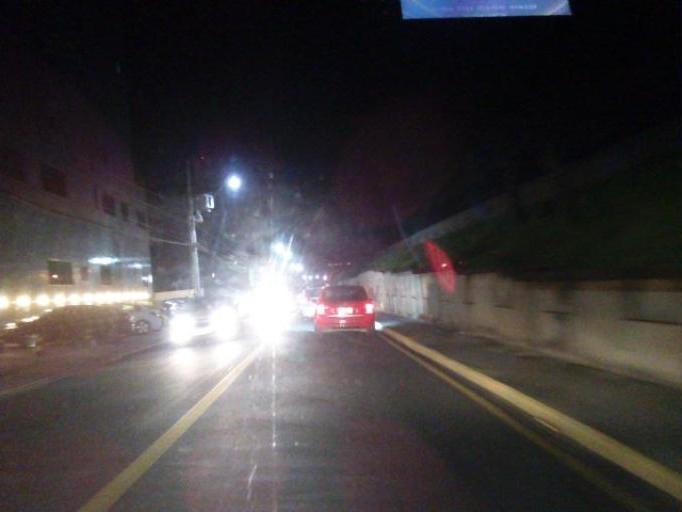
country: BR
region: Santa Catarina
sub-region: Itapema
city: Itapema
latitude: -27.1093
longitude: -48.6122
